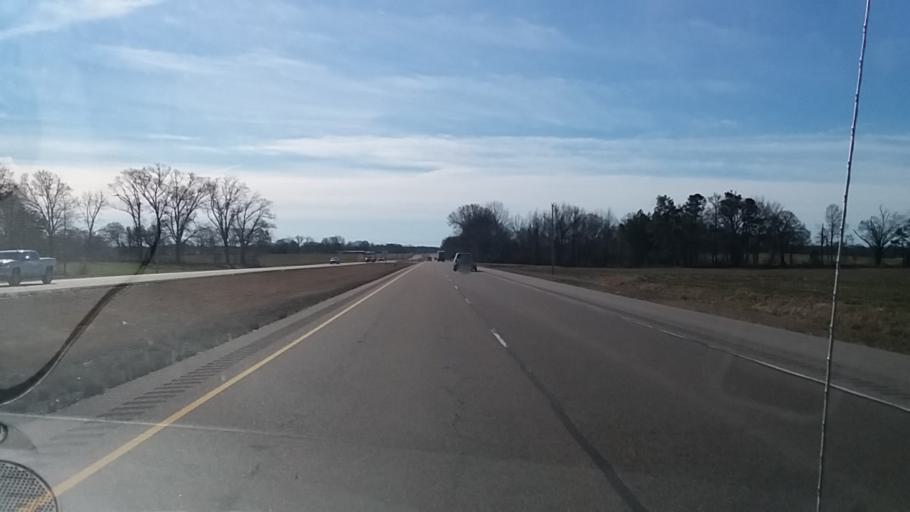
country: US
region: Tennessee
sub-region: Crockett County
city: Alamo
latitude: 35.8698
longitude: -89.2148
